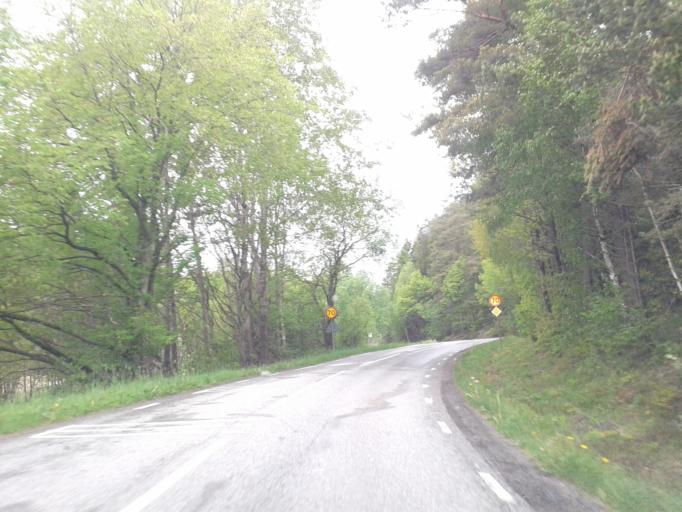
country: SE
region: Vaestra Goetaland
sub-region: Kungalvs Kommun
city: Kode
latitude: 57.8487
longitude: 11.7860
